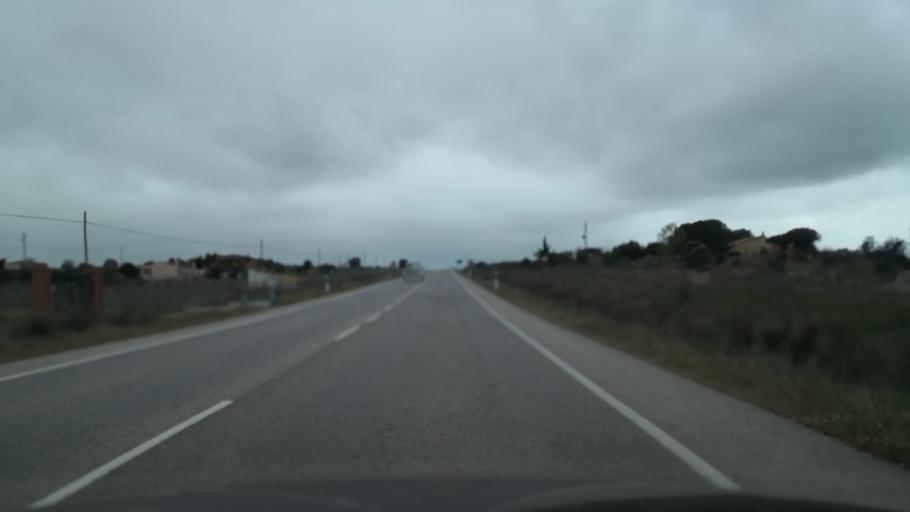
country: ES
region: Extremadura
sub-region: Provincia de Caceres
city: Malpartida de Caceres
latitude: 39.3841
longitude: -6.4413
